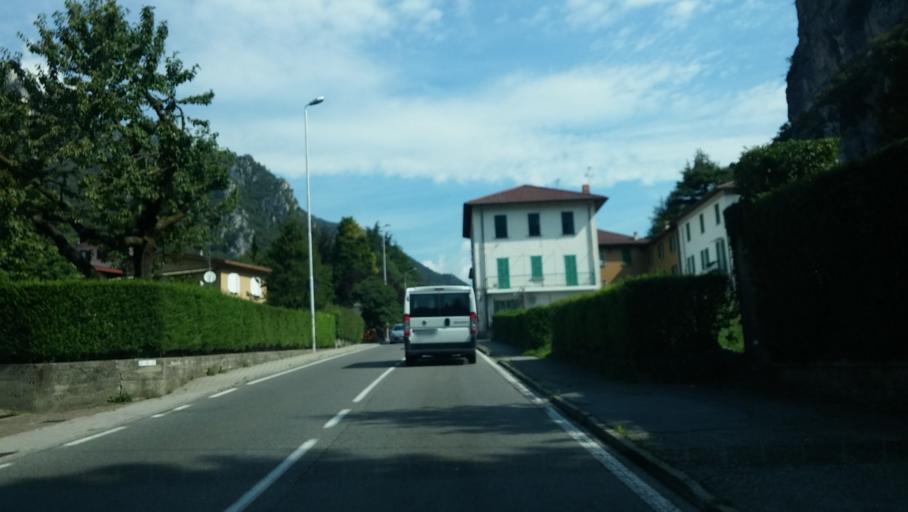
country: IT
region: Lombardy
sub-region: Provincia di Lecco
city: Ballabio
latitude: 45.8996
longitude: 9.4266
